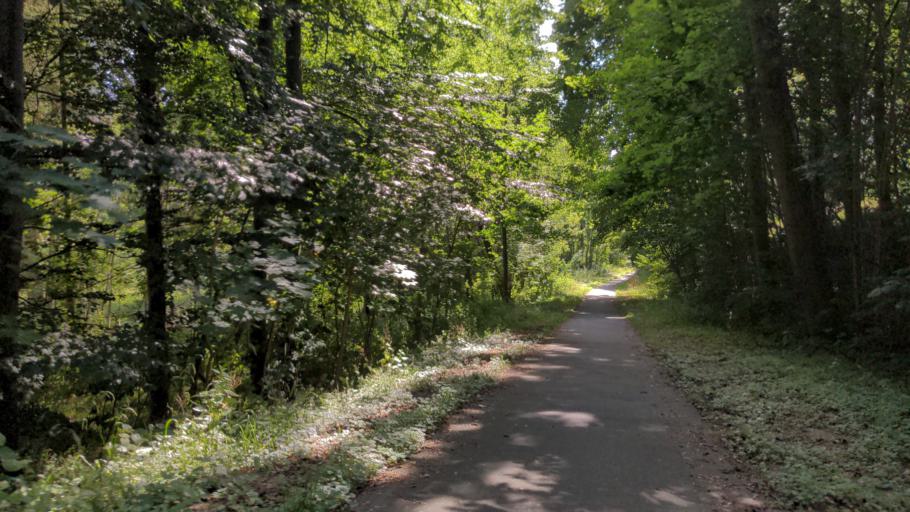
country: DE
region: Schleswig-Holstein
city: Rathjensdorf
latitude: 54.1857
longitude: 10.4528
